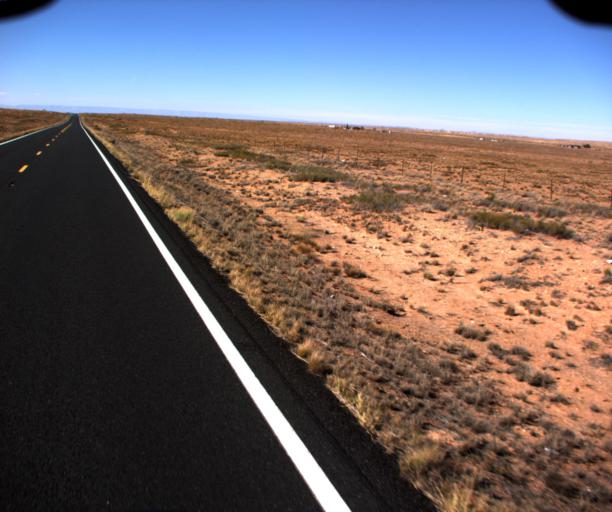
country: US
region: Arizona
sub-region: Coconino County
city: Tuba City
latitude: 36.0176
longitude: -111.1049
